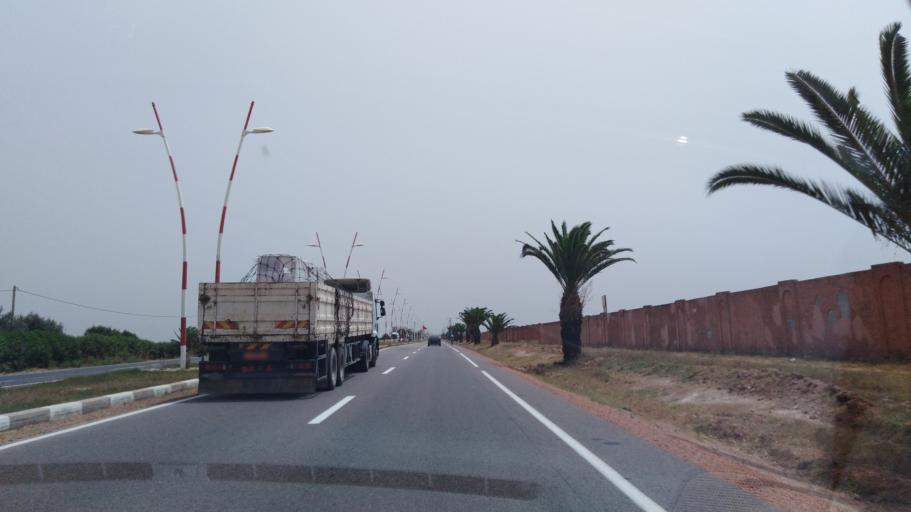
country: MA
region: Chaouia-Ouardigha
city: Nouaseur
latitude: 33.3936
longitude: -7.5966
